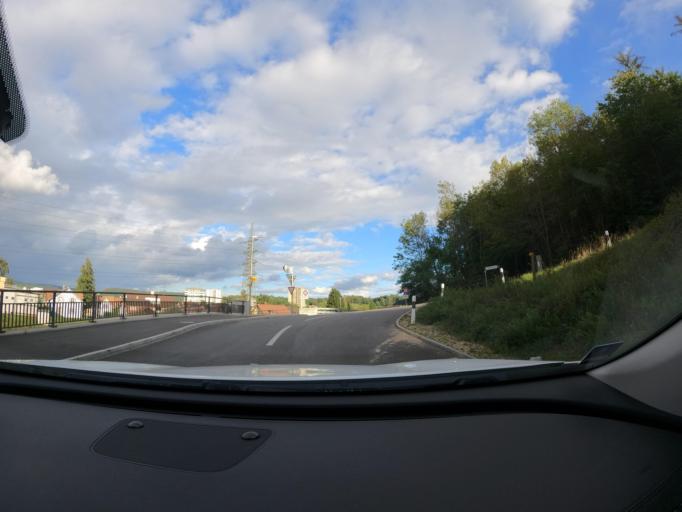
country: CH
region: Aargau
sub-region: Bezirk Brugg
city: Brugg
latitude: 47.4740
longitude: 8.2049
